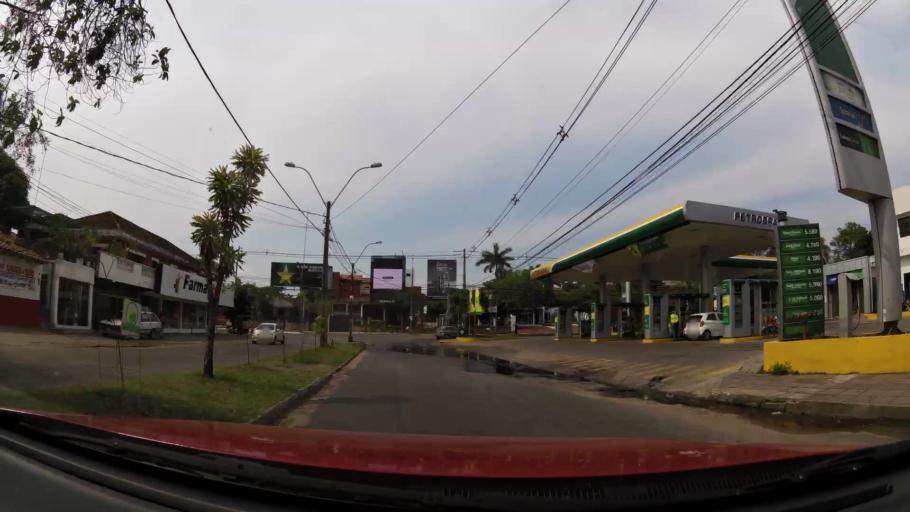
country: PY
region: Asuncion
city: Asuncion
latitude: -25.2761
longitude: -57.5674
